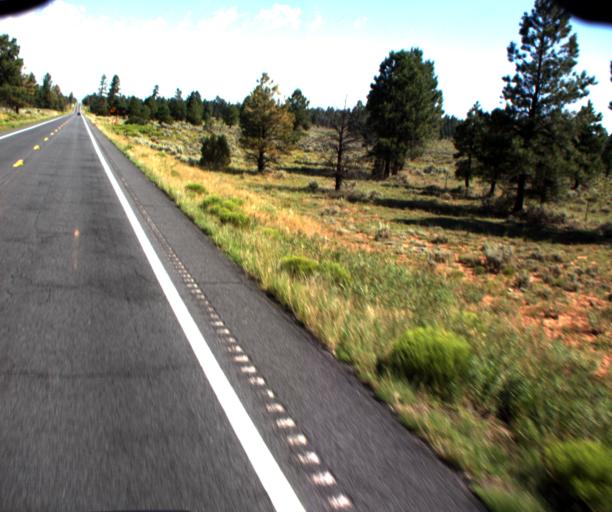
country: US
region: Arizona
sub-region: Coconino County
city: Grand Canyon Village
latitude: 35.9198
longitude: -112.1301
